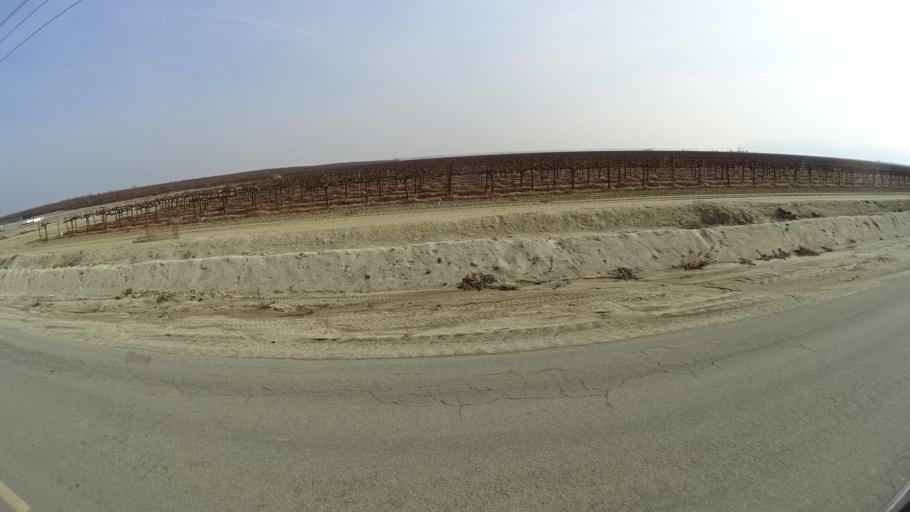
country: US
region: California
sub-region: Kern County
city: Greenfield
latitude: 35.0898
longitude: -119.1007
